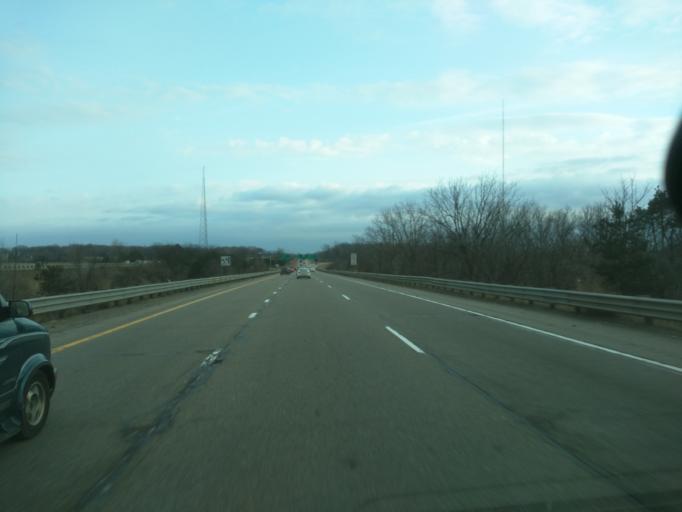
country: US
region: Michigan
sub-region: Ingham County
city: Holt
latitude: 42.6826
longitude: -84.5010
